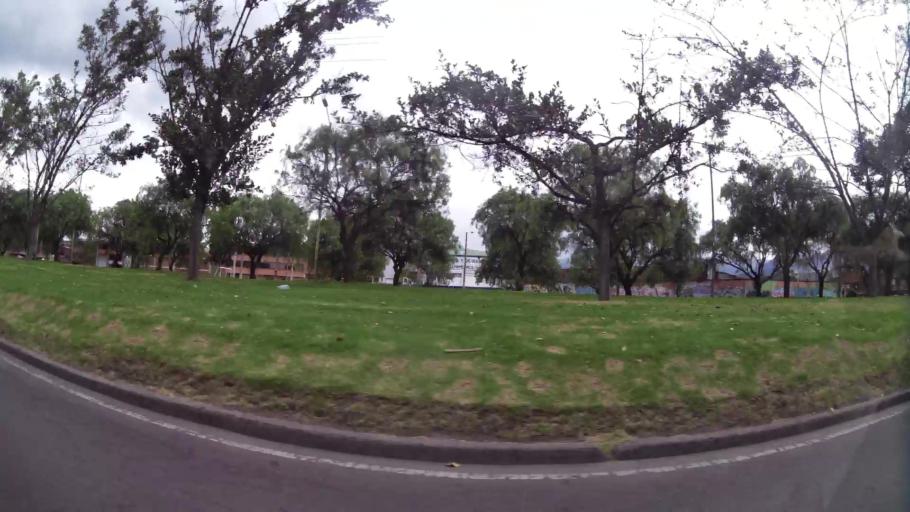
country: CO
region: Bogota D.C.
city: Bogota
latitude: 4.6238
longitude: -74.1068
